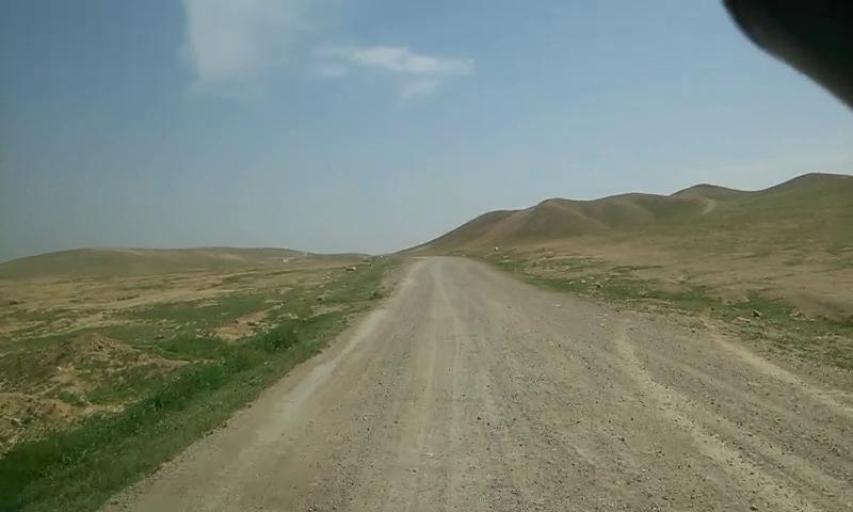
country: PS
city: `Arab ar Rashaydah
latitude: 31.5306
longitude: 35.2869
